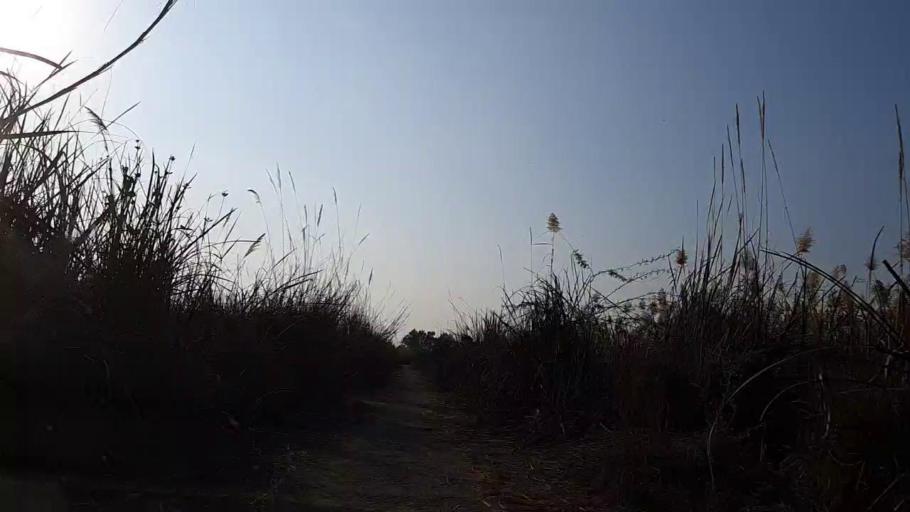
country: PK
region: Sindh
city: Sakrand
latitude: 26.0935
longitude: 68.3777
